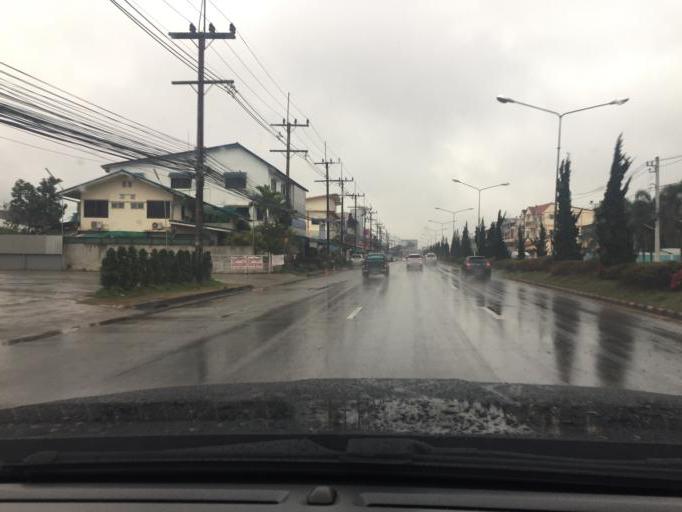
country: TH
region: Chiang Rai
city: Chiang Rai
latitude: 19.9702
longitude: 99.8573
